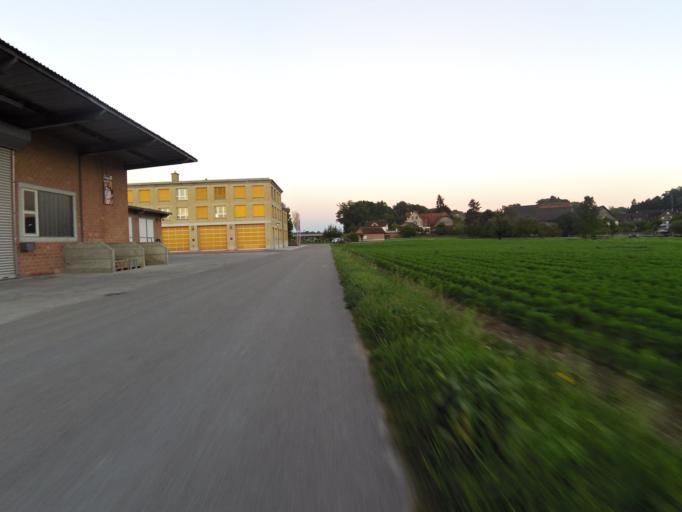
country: CH
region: Thurgau
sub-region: Weinfelden District
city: Maerstetten-Dorf
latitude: 47.5724
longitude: 9.0575
